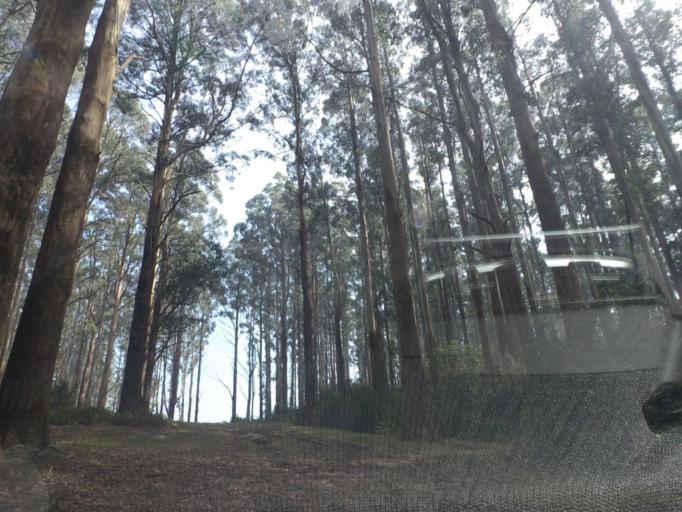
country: AU
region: Victoria
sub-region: Yarra Ranges
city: Healesville
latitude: -37.5667
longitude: 145.6013
